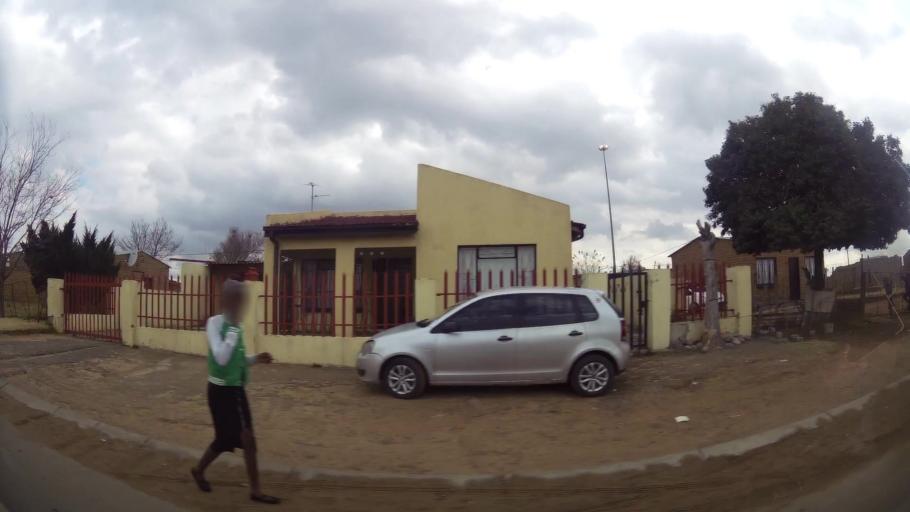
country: ZA
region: Orange Free State
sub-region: Fezile Dabi District Municipality
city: Sasolburg
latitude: -26.8563
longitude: 27.8765
